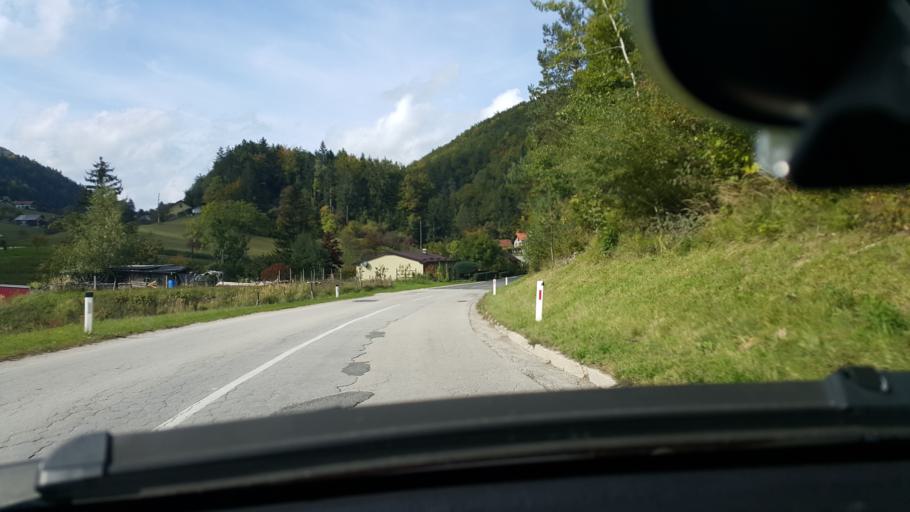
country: SI
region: Zrece
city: Zrece
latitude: 46.3691
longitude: 15.3474
